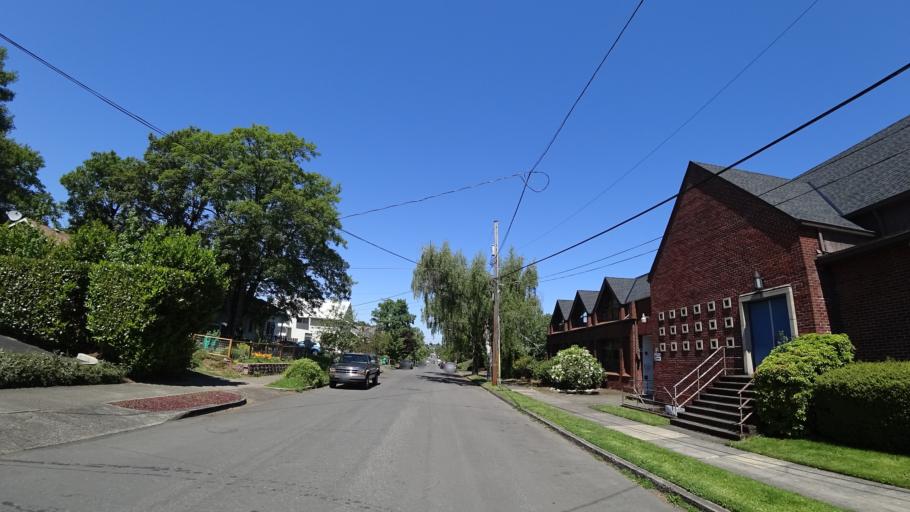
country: US
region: Oregon
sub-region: Multnomah County
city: Lents
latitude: 45.4978
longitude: -122.6071
